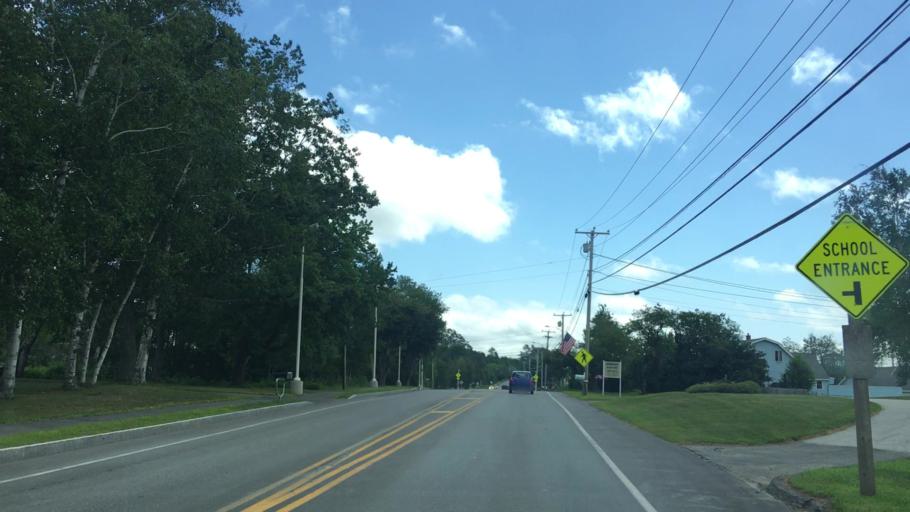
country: US
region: Maine
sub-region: Penobscot County
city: Hermon
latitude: 44.8070
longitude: -68.9047
